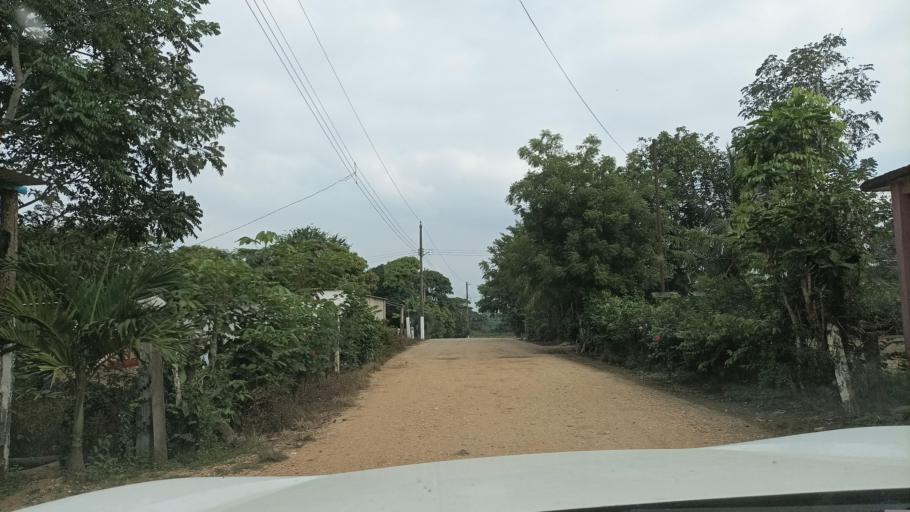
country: MX
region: Veracruz
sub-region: Texistepec
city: San Lorenzo Tenochtitlan
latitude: 17.7734
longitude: -94.8045
